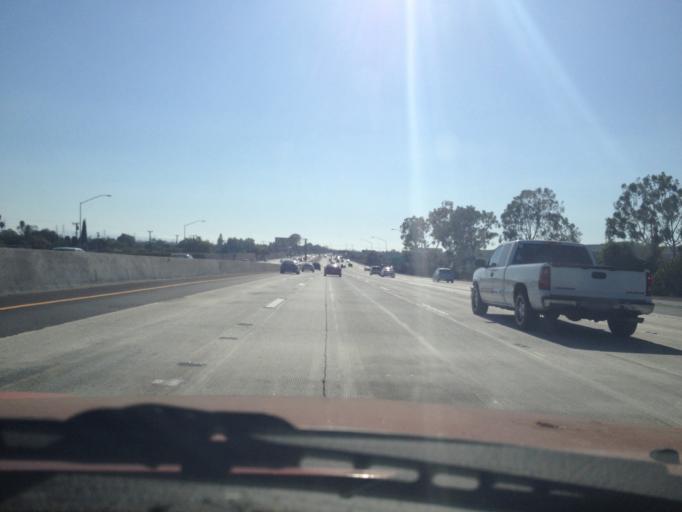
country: US
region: California
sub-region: Orange County
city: Buena Park
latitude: 33.8561
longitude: -118.0130
